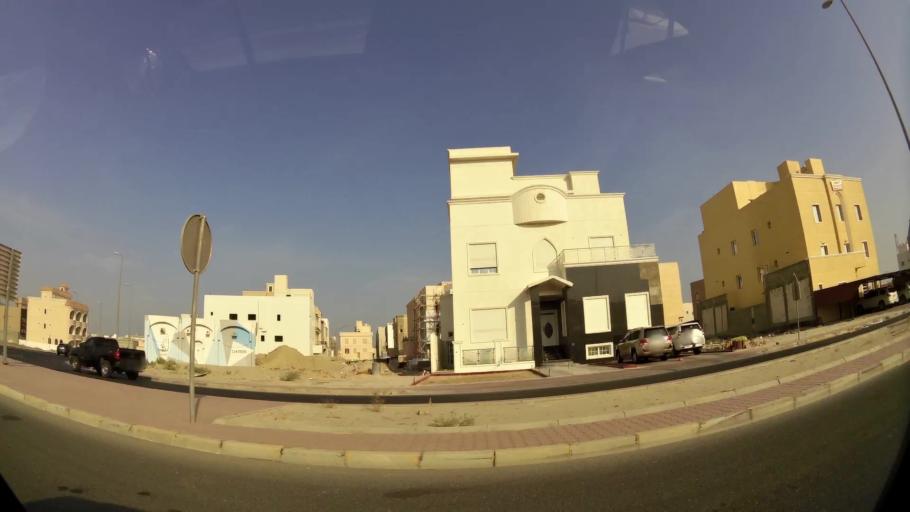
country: KW
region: Mubarak al Kabir
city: Mubarak al Kabir
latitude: 29.1969
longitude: 48.1029
